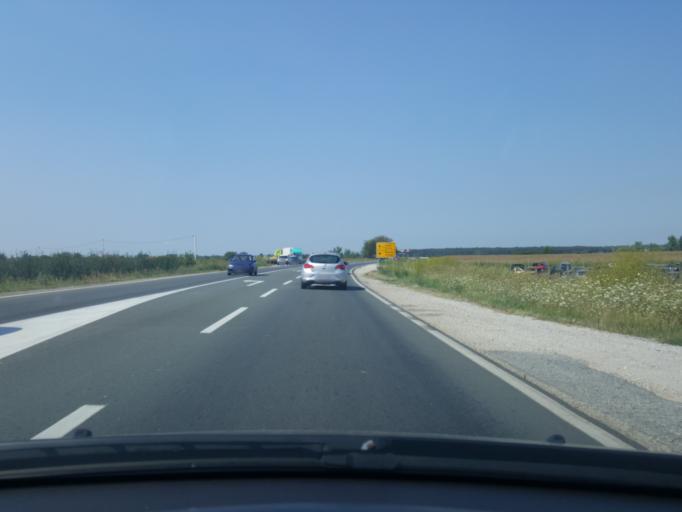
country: RS
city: Klenak
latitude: 44.7840
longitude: 19.7233
